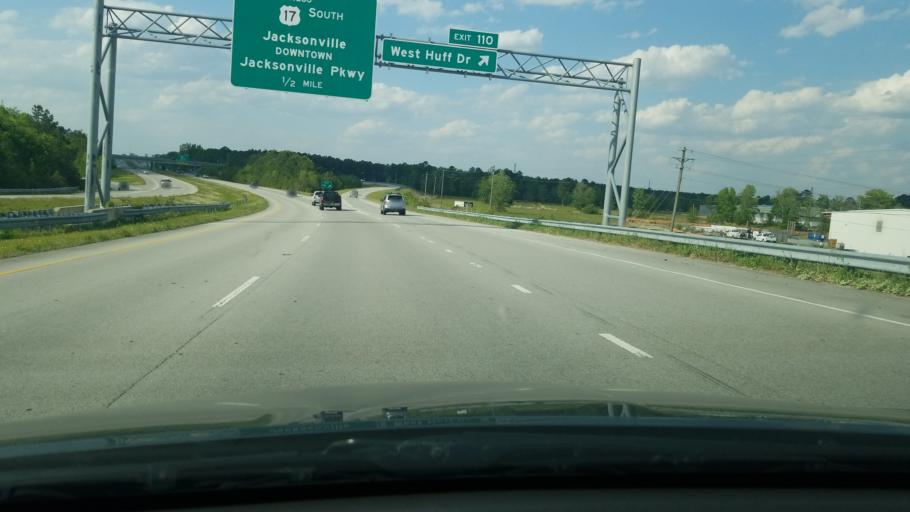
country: US
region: North Carolina
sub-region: Onslow County
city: Jacksonville
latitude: 34.7592
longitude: -77.3945
